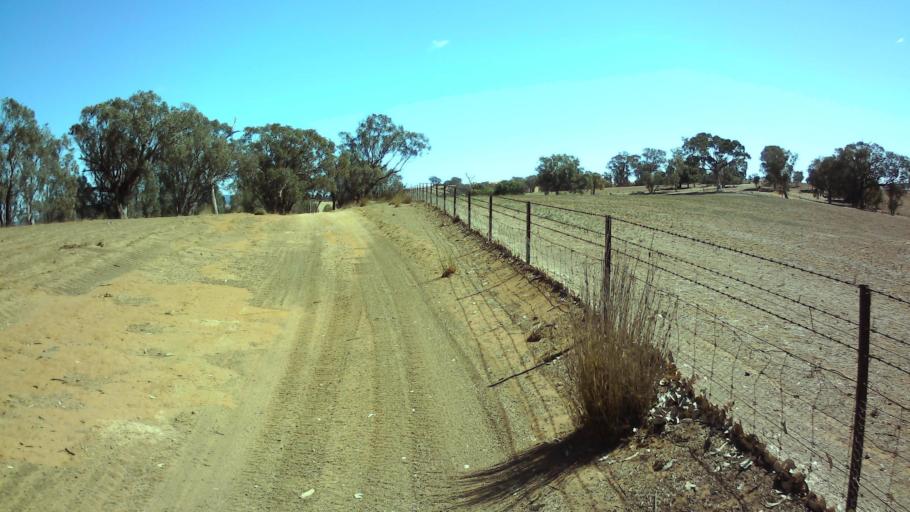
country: AU
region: New South Wales
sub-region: Weddin
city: Grenfell
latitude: -33.9935
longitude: 148.4367
